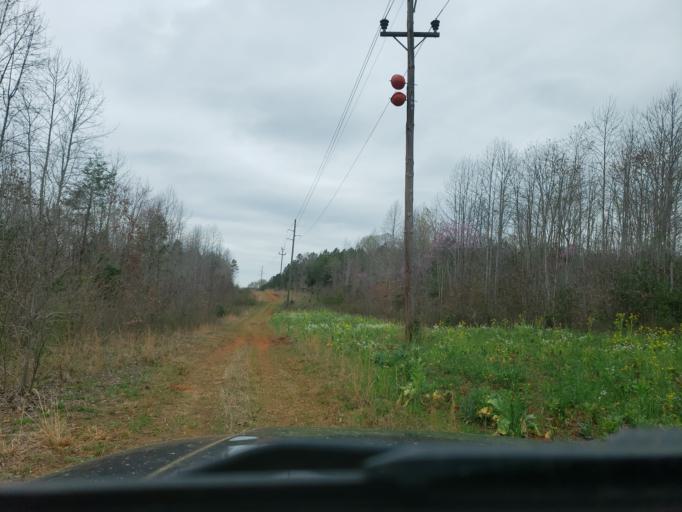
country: US
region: North Carolina
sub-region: Cleveland County
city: White Plains
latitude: 35.1873
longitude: -81.3707
